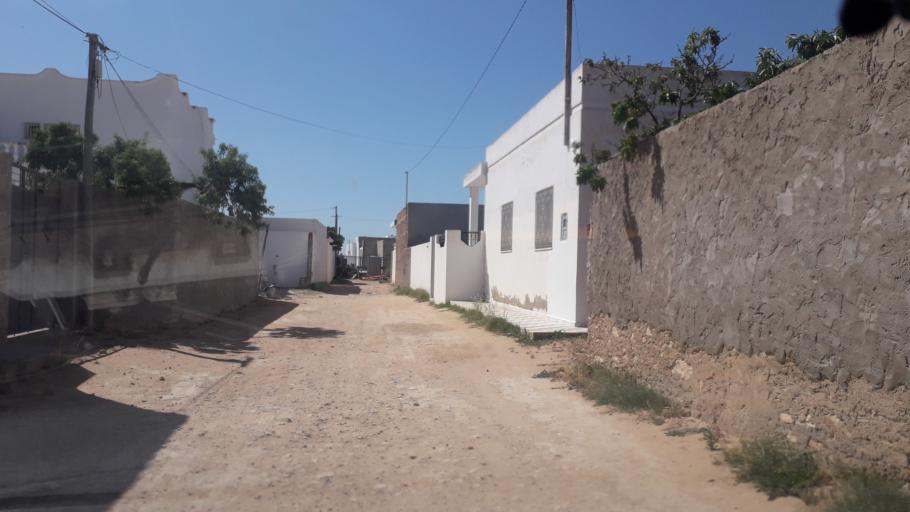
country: TN
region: Safaqis
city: Al Qarmadah
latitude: 34.8317
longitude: 10.7664
